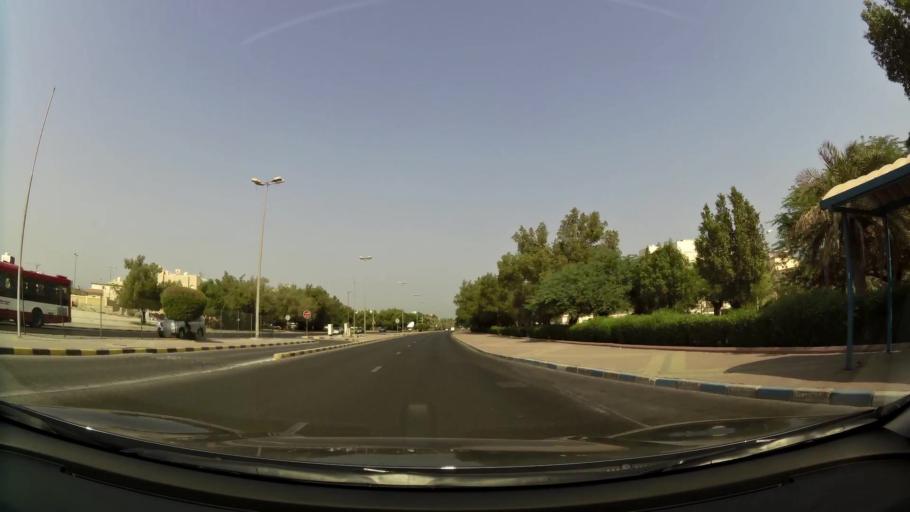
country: KW
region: Al Asimah
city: Ad Dasmah
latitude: 29.3528
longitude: 48.0155
